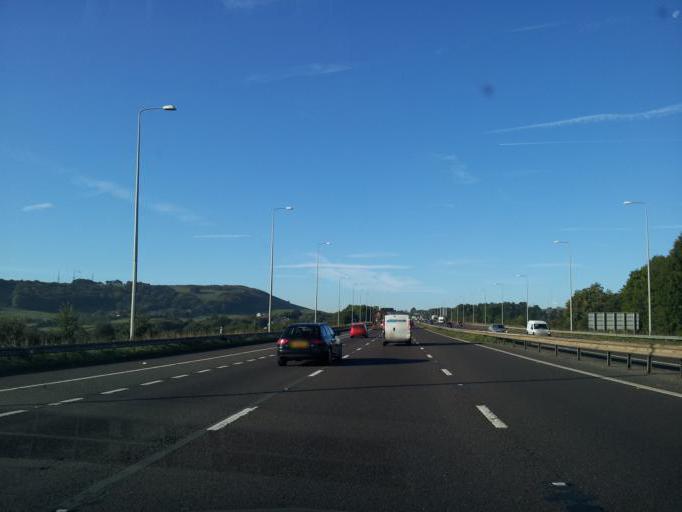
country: GB
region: England
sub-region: Kirklees
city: Linthwaite
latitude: 53.6569
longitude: -1.8698
